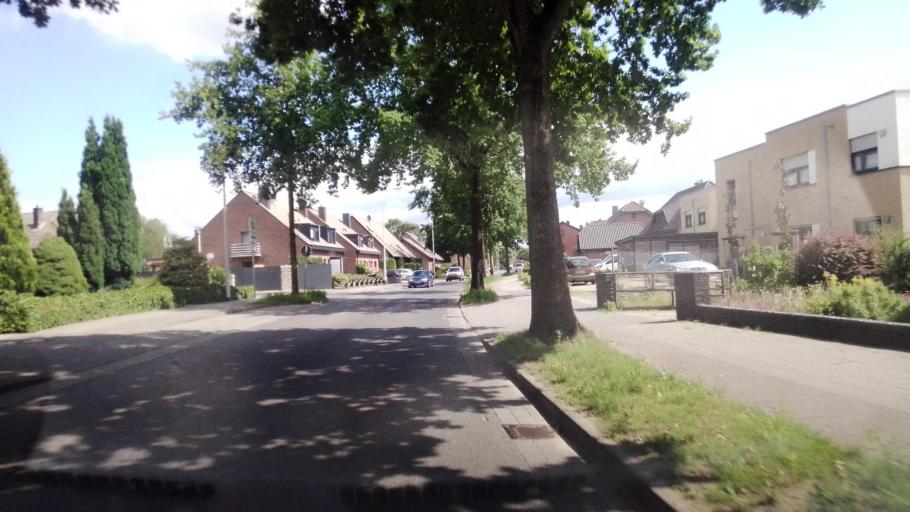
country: NL
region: Limburg
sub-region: Gemeente Venlo
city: Venlo
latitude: 51.3240
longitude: 6.1853
